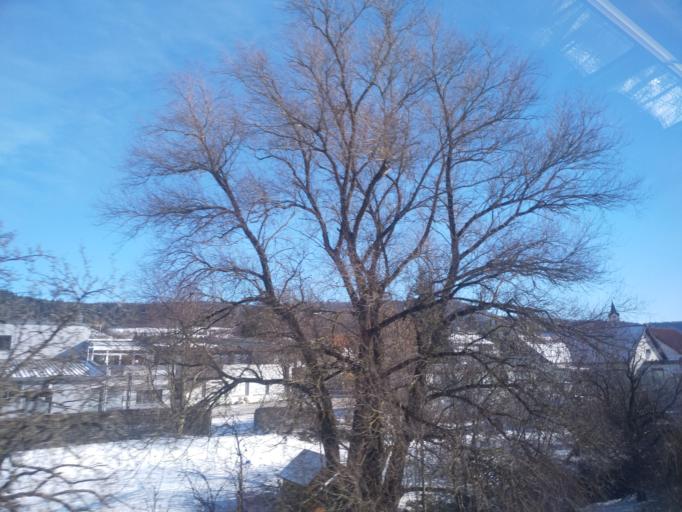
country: DE
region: Baden-Wuerttemberg
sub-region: Freiburg Region
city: Balgheim
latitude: 48.0668
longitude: 8.7583
